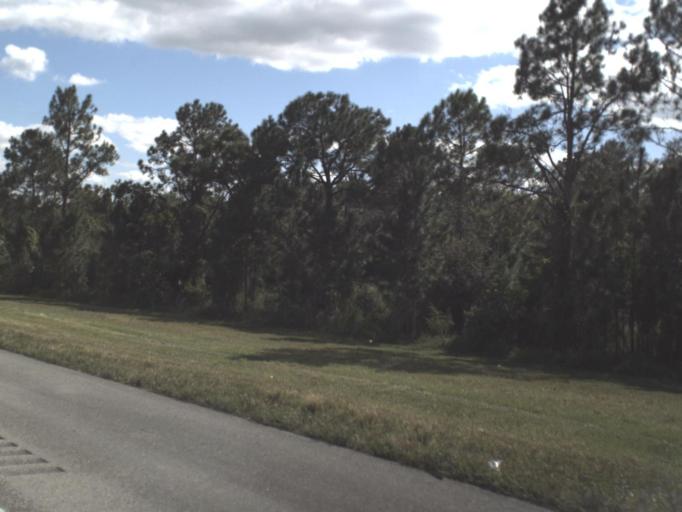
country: US
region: Florida
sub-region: Indian River County
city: Fellsmere
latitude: 27.5979
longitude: -80.8209
